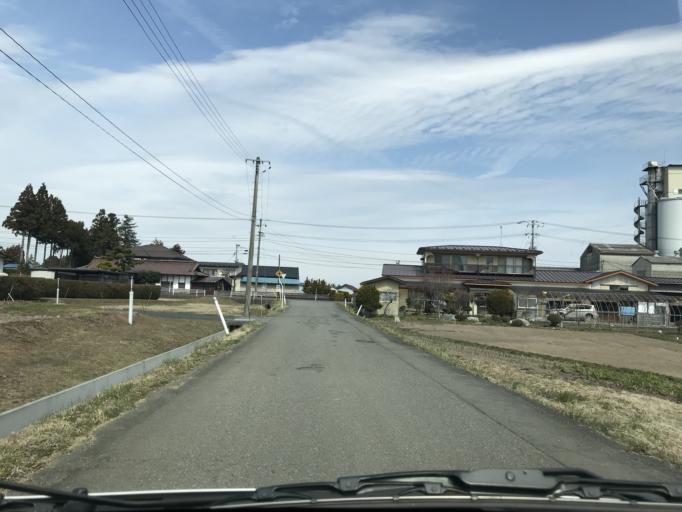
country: JP
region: Iwate
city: Mizusawa
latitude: 39.1393
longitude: 141.0830
